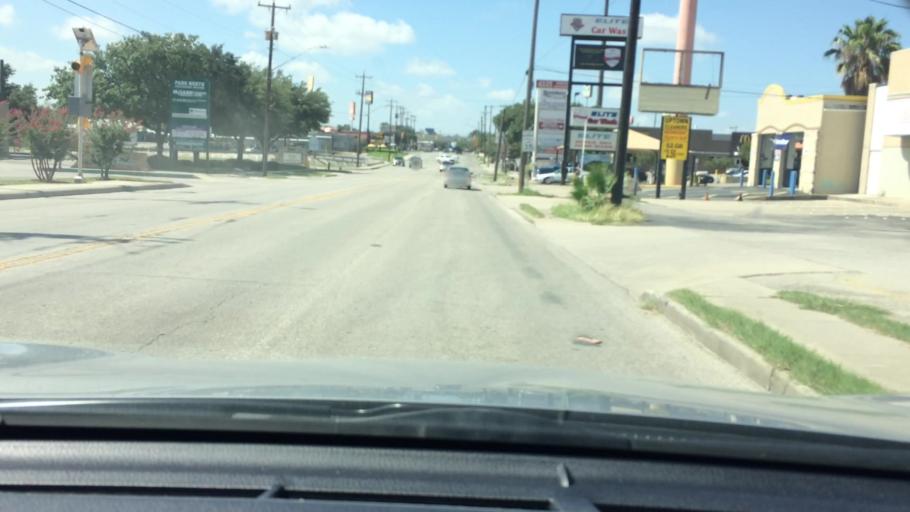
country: US
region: Texas
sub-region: Bexar County
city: Castle Hills
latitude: 29.5153
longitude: -98.5352
